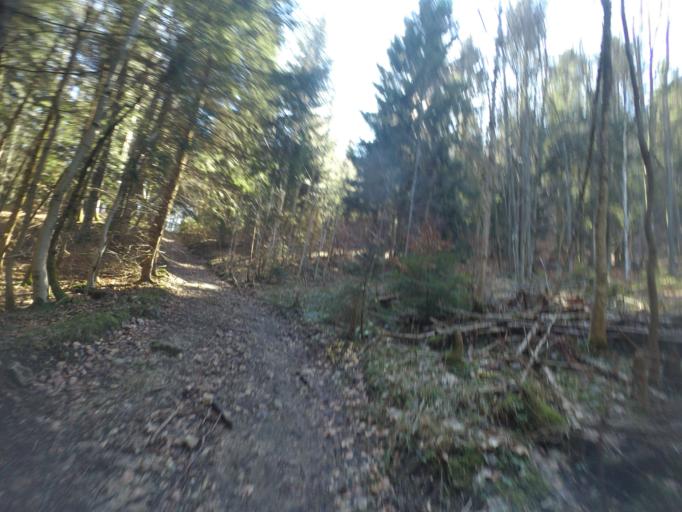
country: AT
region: Salzburg
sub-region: Politischer Bezirk Salzburg-Umgebung
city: Koppl
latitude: 47.8045
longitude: 13.1299
